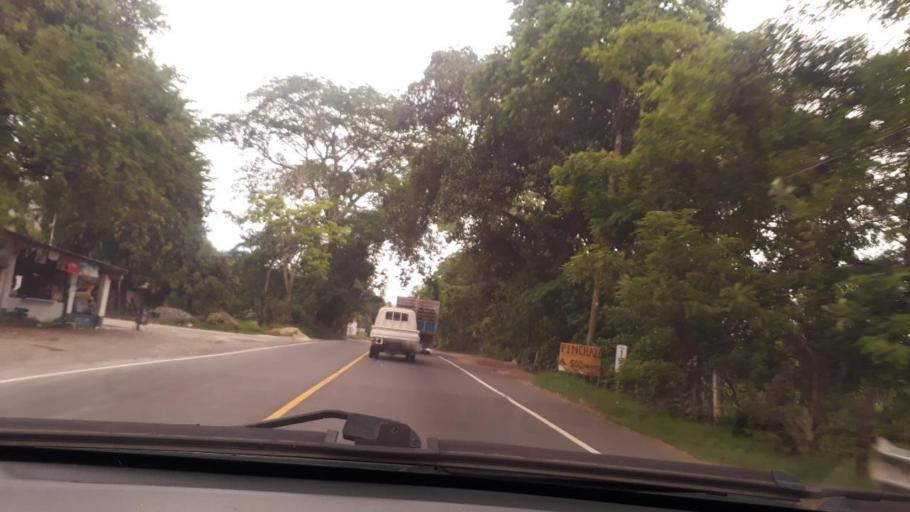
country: GT
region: Izabal
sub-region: Municipio de Los Amates
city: Los Amates
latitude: 15.2399
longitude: -89.1728
